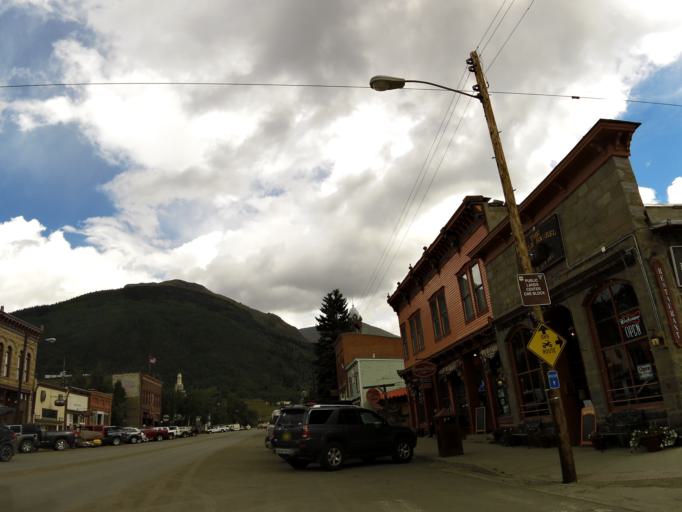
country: US
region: Colorado
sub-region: San Juan County
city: Silverton
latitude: 37.8125
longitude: -107.6635
